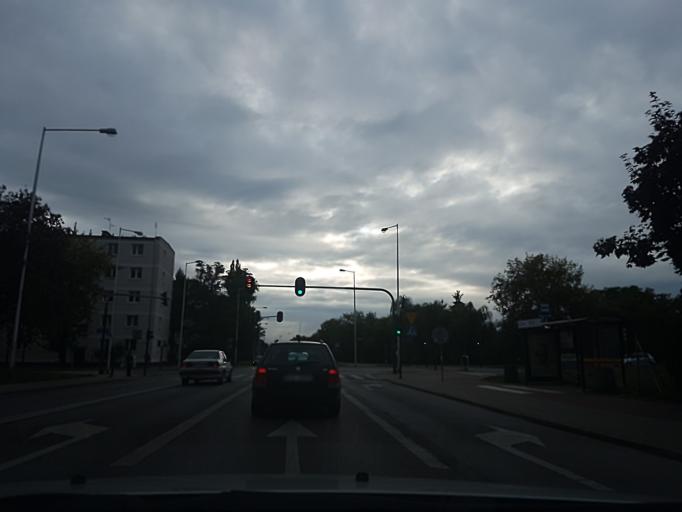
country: PL
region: Lodz Voivodeship
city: Lodz
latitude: 51.7812
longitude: 19.4274
